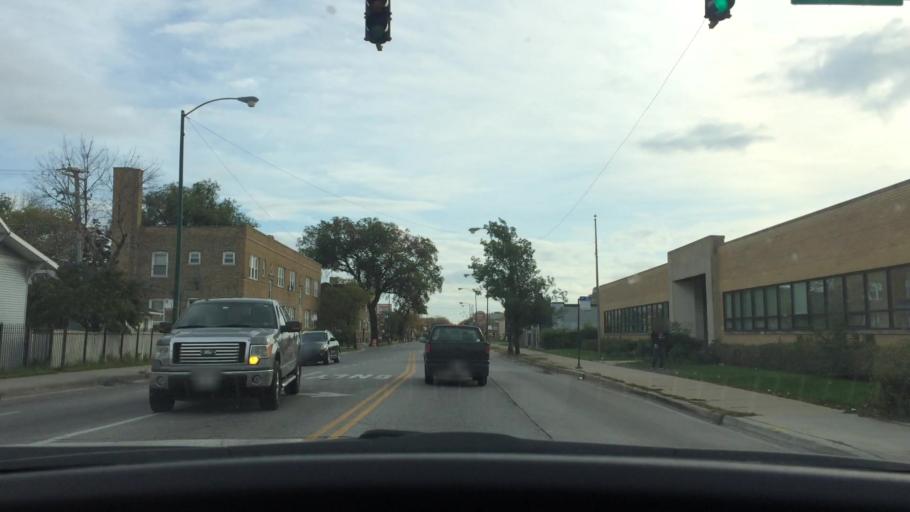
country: US
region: Illinois
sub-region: Cook County
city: Lincolnwood
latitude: 41.9466
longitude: -87.7127
